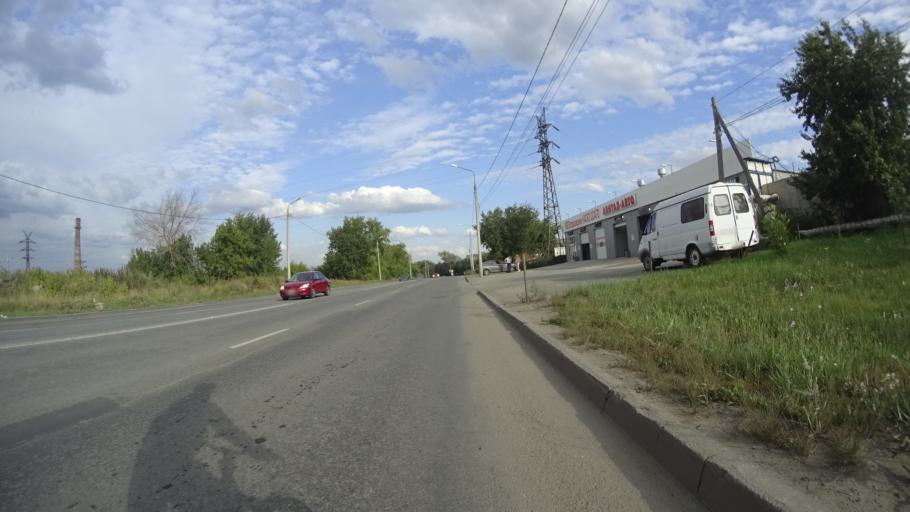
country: RU
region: Chelyabinsk
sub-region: Gorod Chelyabinsk
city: Chelyabinsk
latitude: 55.1967
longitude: 61.3733
